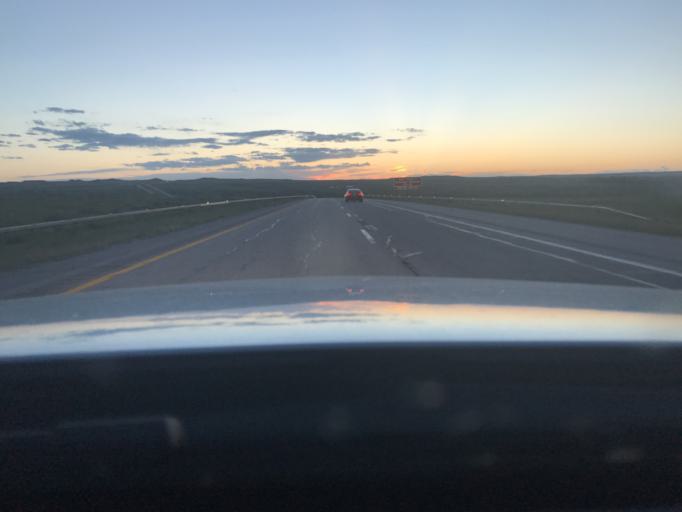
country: US
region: Wyoming
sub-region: Converse County
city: Glenrock
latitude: 42.8356
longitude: -105.8528
